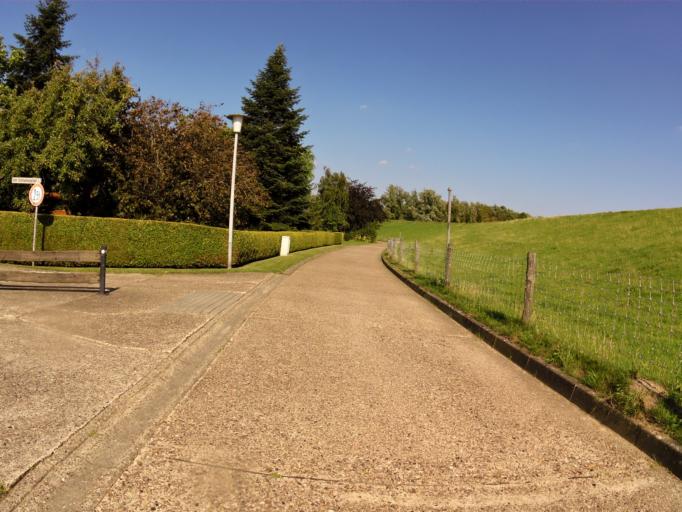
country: DE
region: Lower Saxony
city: Brake (Unterweser)
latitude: 53.4069
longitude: 8.4661
